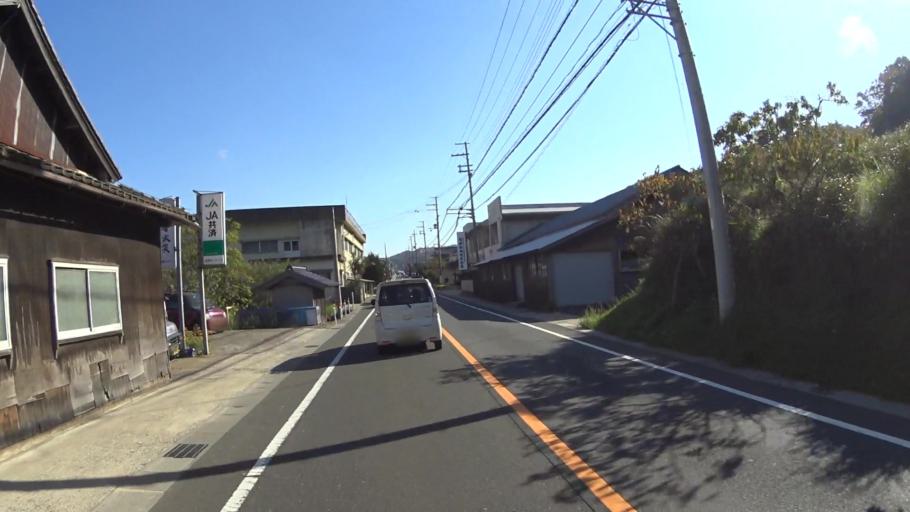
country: JP
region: Kyoto
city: Miyazu
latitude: 35.6628
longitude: 135.0305
